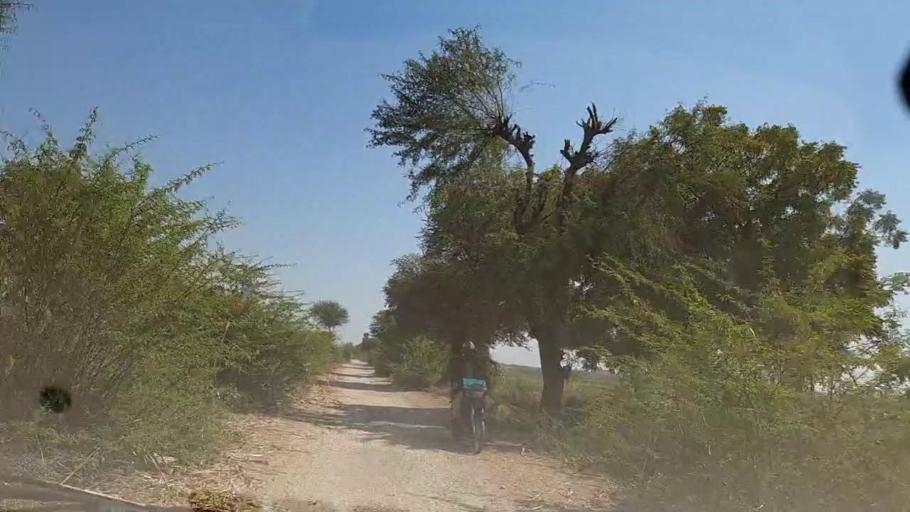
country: PK
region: Sindh
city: Mirpur Khas
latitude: 25.4271
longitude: 69.0305
